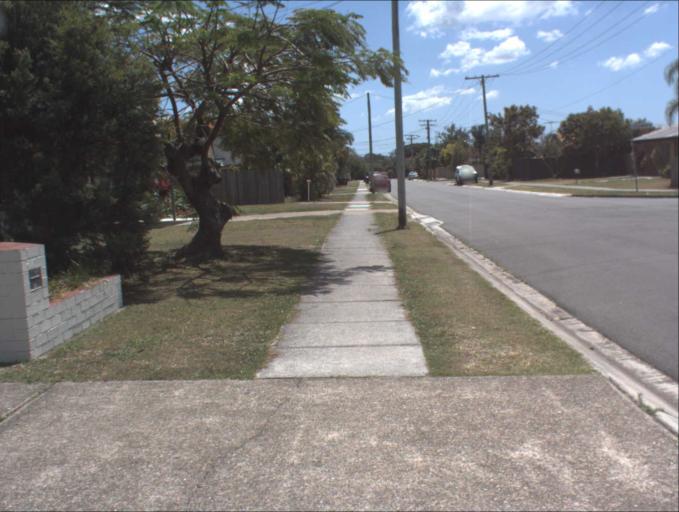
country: AU
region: Queensland
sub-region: Logan
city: Windaroo
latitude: -27.7309
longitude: 153.2093
